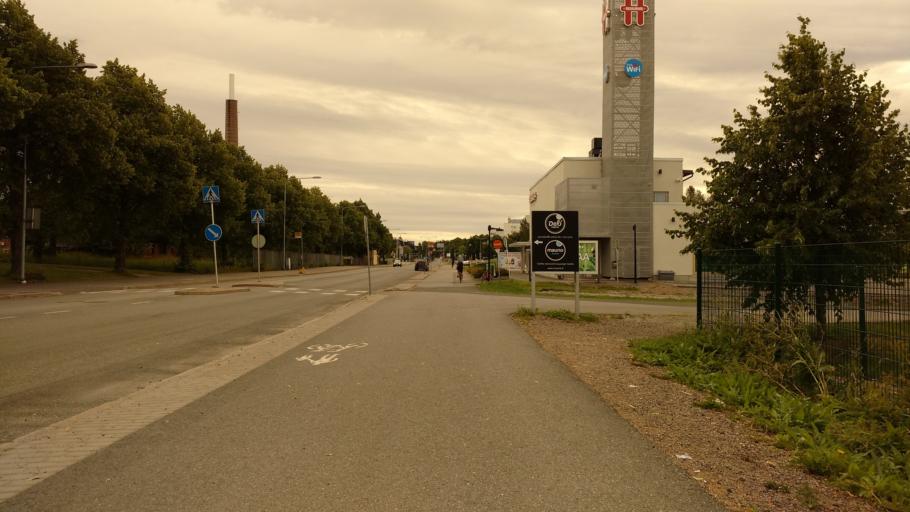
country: FI
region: Varsinais-Suomi
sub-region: Turku
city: Turku
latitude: 60.4458
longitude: 22.3004
